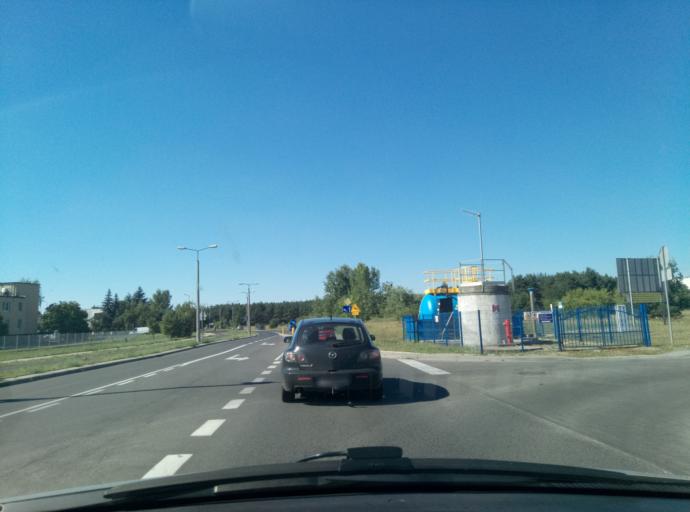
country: PL
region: Kujawsko-Pomorskie
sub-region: Torun
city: Torun
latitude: 53.0418
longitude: 18.5971
